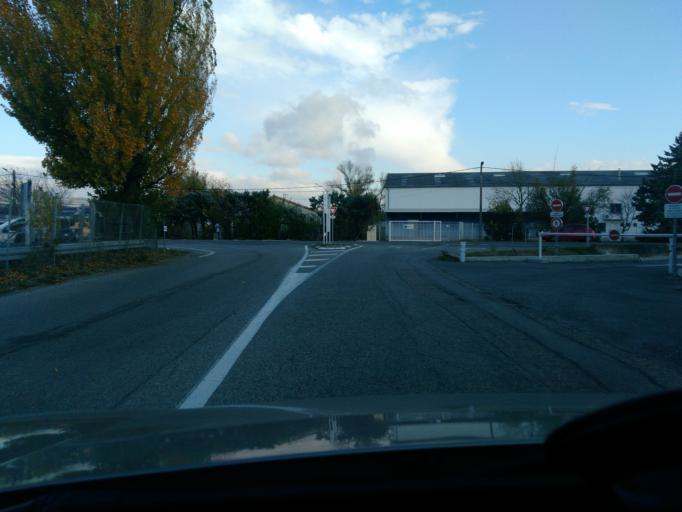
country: FR
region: Rhone-Alpes
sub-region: Departement de la Drome
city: Montelimar
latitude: 44.5717
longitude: 4.7416
